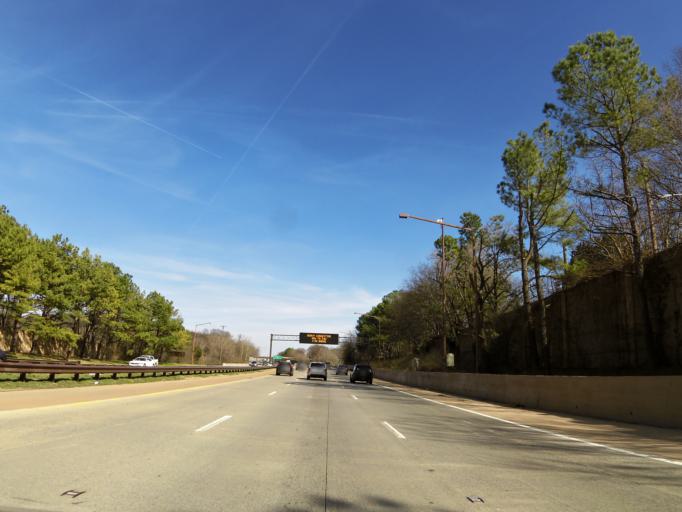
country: US
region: Tennessee
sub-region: Davidson County
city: Oak Hill
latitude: 36.1242
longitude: -86.7409
